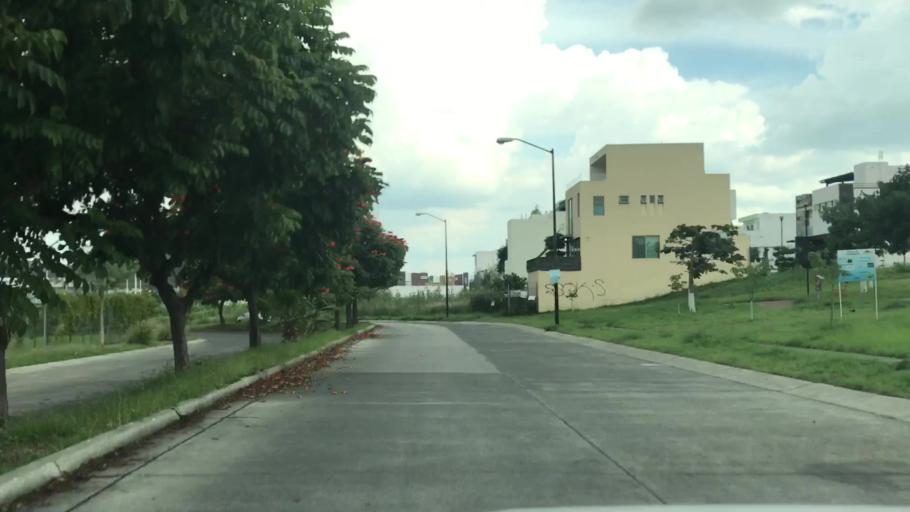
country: MX
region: Jalisco
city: Guadalajara
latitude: 20.6177
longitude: -103.3983
